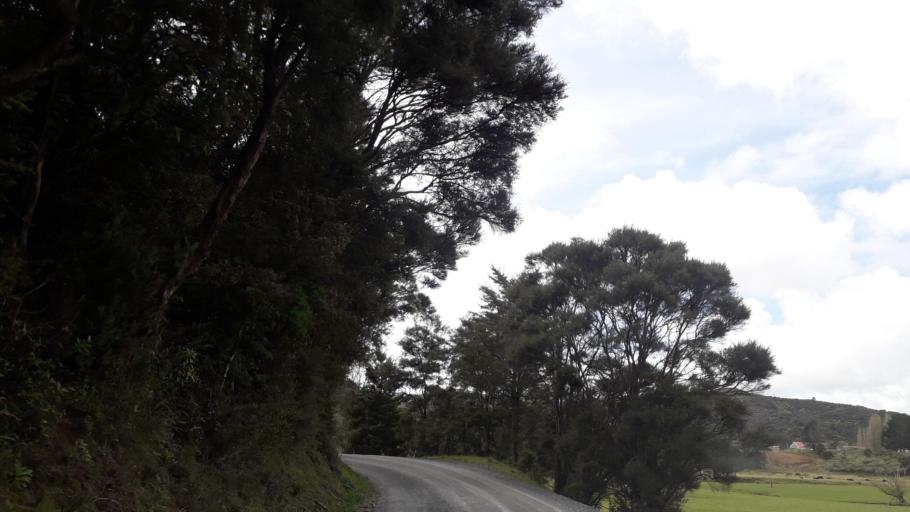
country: NZ
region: Northland
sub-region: Far North District
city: Taipa
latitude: -35.0486
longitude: 173.5600
